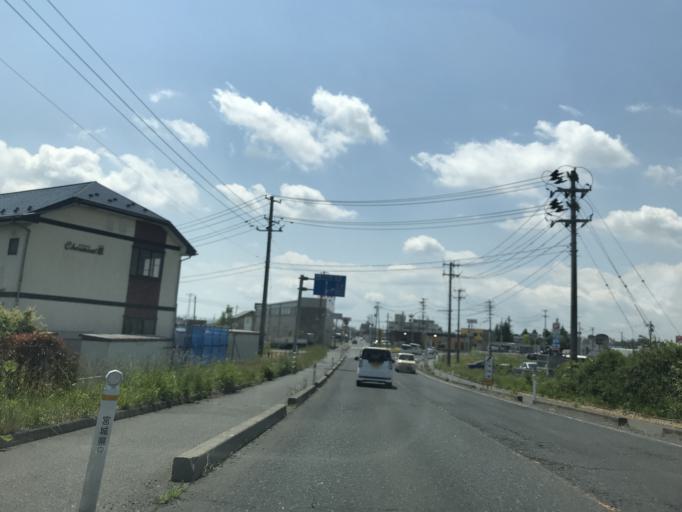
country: JP
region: Miyagi
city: Kogota
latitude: 38.5477
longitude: 141.0610
